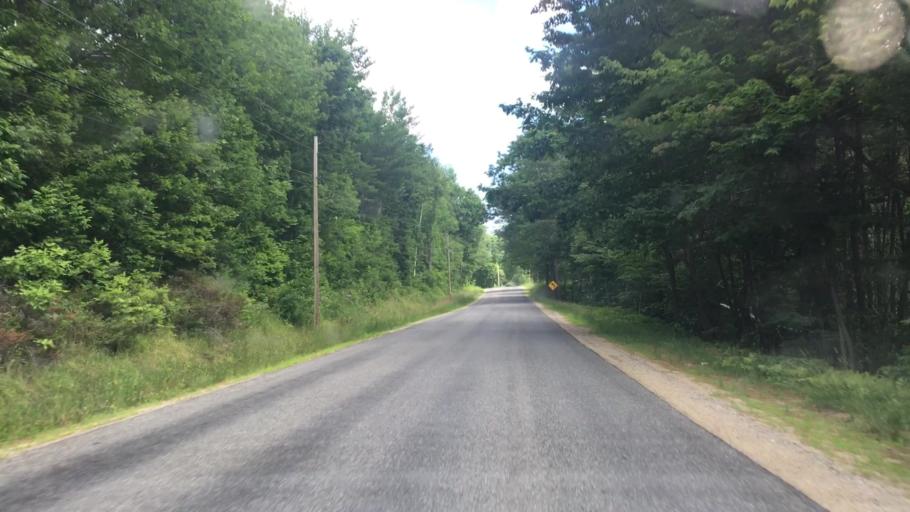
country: US
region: Maine
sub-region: Franklin County
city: Jay
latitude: 44.5357
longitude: -70.2125
